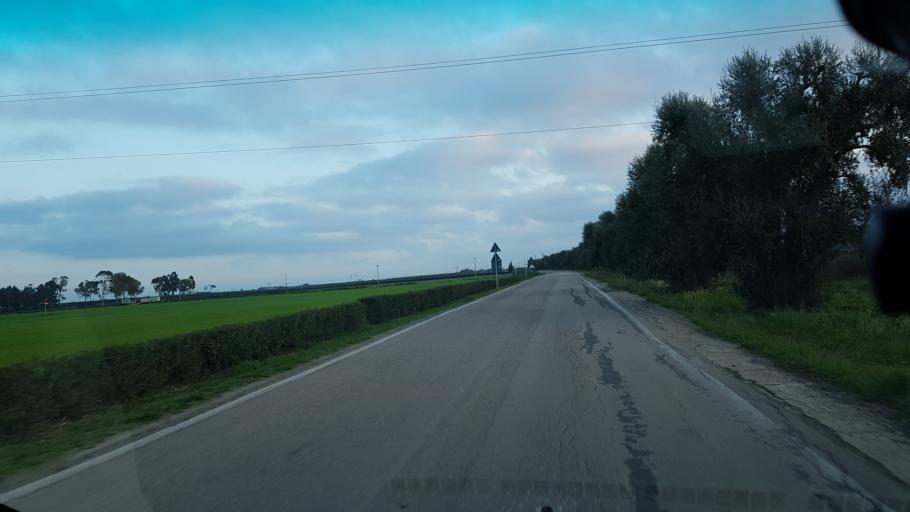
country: IT
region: Apulia
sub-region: Provincia di Brindisi
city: Mesagne
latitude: 40.6051
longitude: 17.7916
